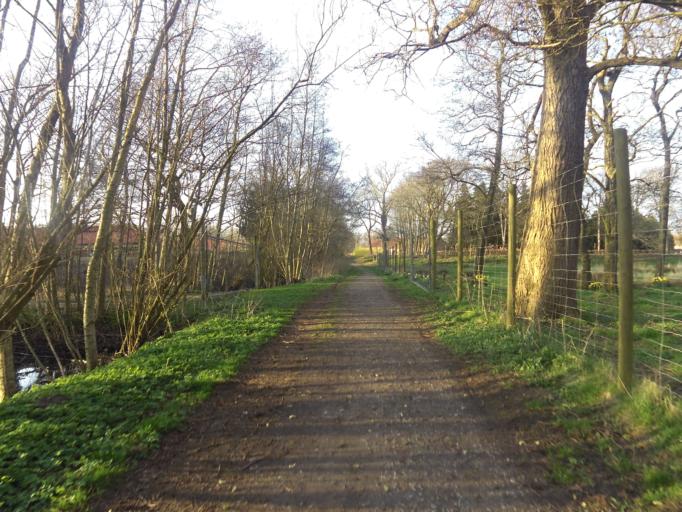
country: DK
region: South Denmark
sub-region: Esbjerg Kommune
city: Ribe
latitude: 55.3231
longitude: 8.7760
